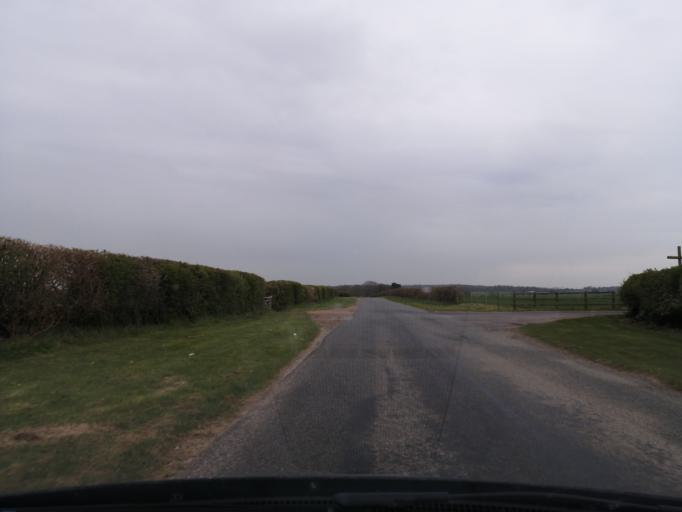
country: GB
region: England
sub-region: Peterborough
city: Wittering
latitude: 52.6077
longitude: -0.4619
